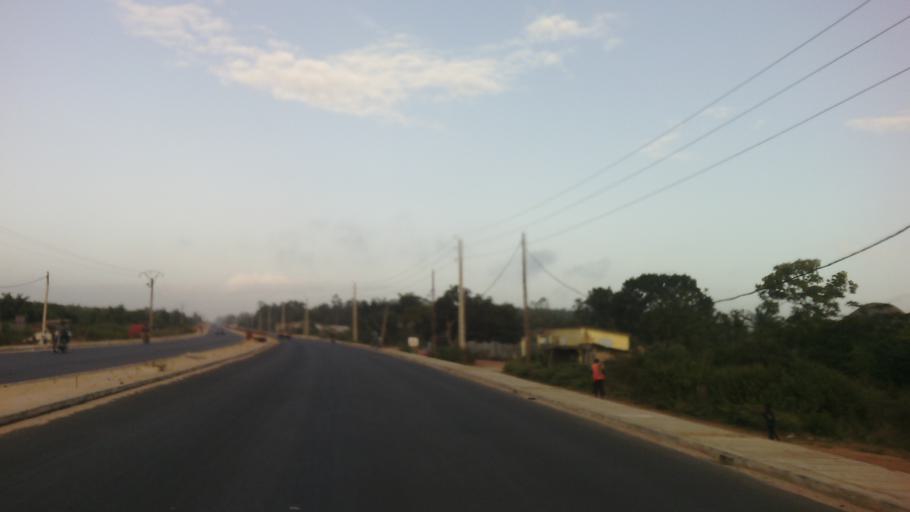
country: BJ
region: Atlantique
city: Hevie
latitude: 6.3819
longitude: 2.1715
